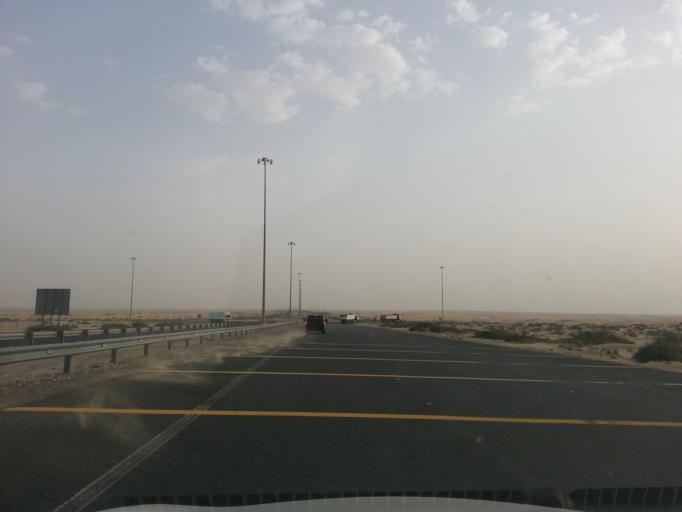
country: AE
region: Dubai
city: Dubai
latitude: 24.5952
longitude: 55.1218
